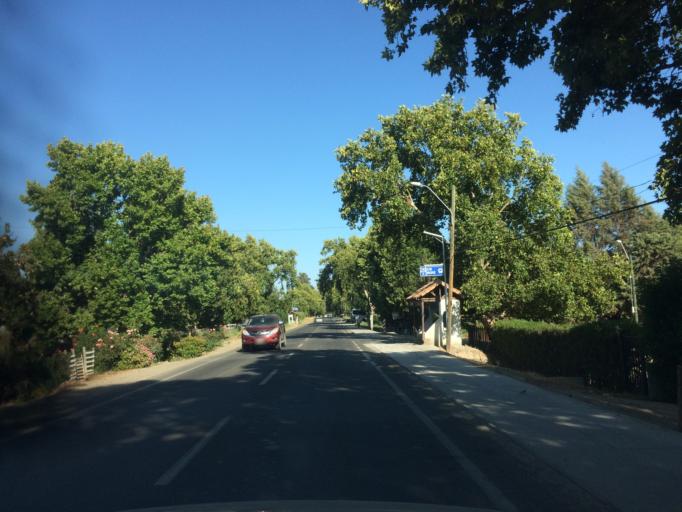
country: CL
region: Santiago Metropolitan
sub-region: Provincia de Melipilla
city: Melipilla
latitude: -33.4916
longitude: -71.1686
